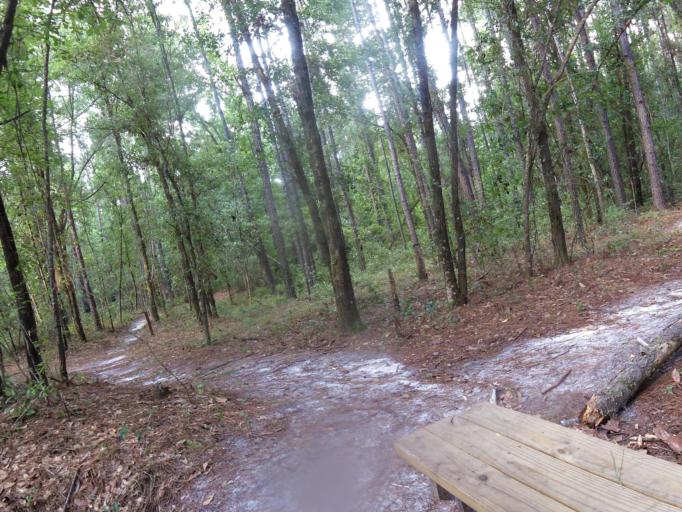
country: US
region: Florida
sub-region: Duval County
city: Jacksonville
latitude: 30.3289
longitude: -81.7795
